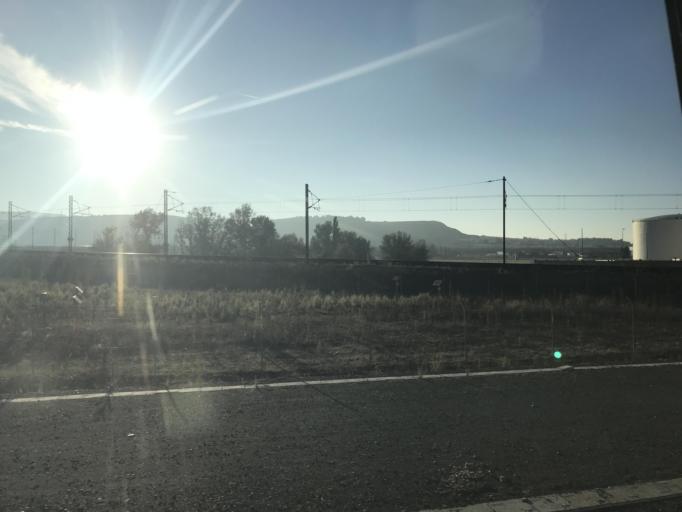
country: ES
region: Castille and Leon
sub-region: Provincia de Valladolid
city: Santovenia de Pisuerga
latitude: 41.6986
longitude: -4.6772
